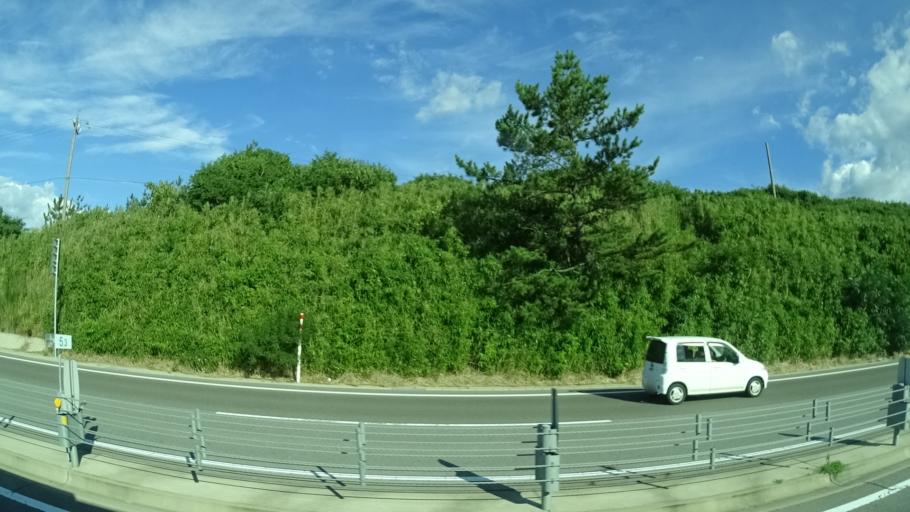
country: JP
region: Ishikawa
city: Kanazawa-shi
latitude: 36.6727
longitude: 136.6506
